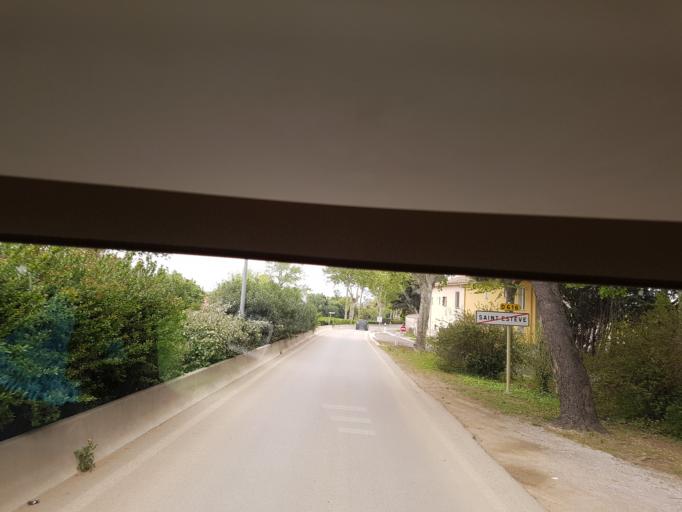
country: FR
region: Languedoc-Roussillon
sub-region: Departement des Pyrenees-Orientales
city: Saint-Esteve
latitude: 42.7103
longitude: 2.8591
